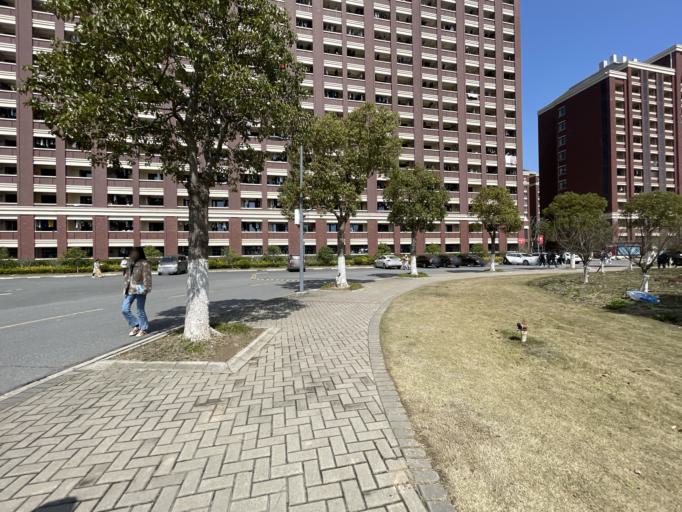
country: CN
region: Shanghai Shi
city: Shuyuan
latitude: 30.8955
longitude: 121.8851
